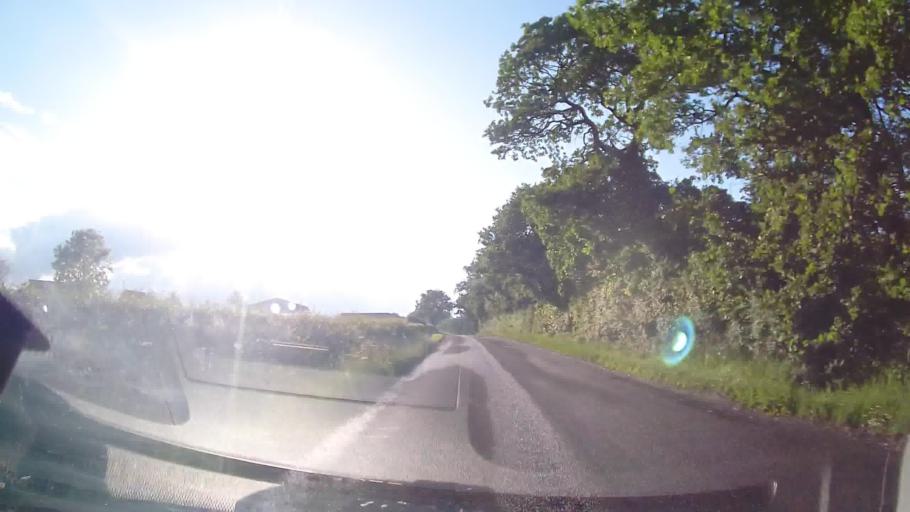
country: GB
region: England
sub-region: Leicestershire
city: Markfield
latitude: 52.6573
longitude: -1.2602
